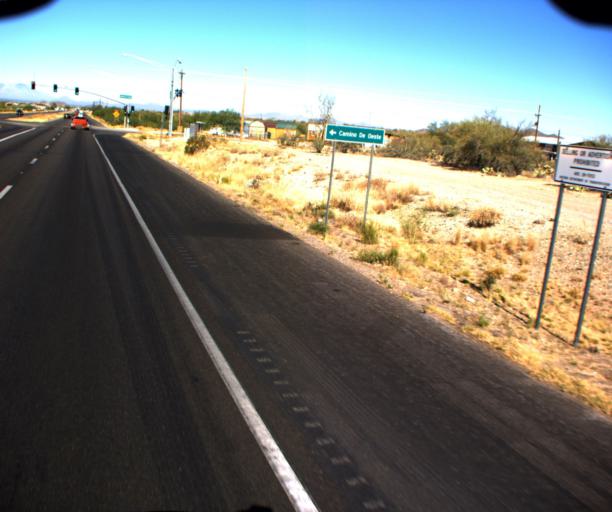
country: US
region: Arizona
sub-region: Pima County
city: Tucson Estates
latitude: 32.1741
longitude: -111.0617
